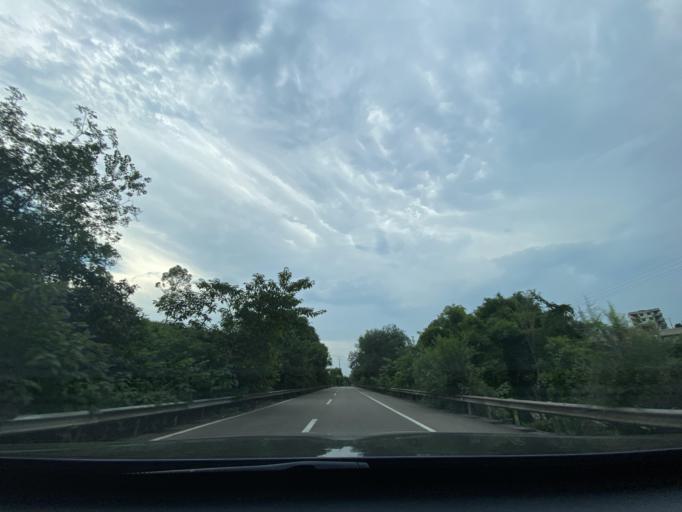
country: CN
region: Sichuan
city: Neijiang
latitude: 29.6790
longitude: 104.9647
